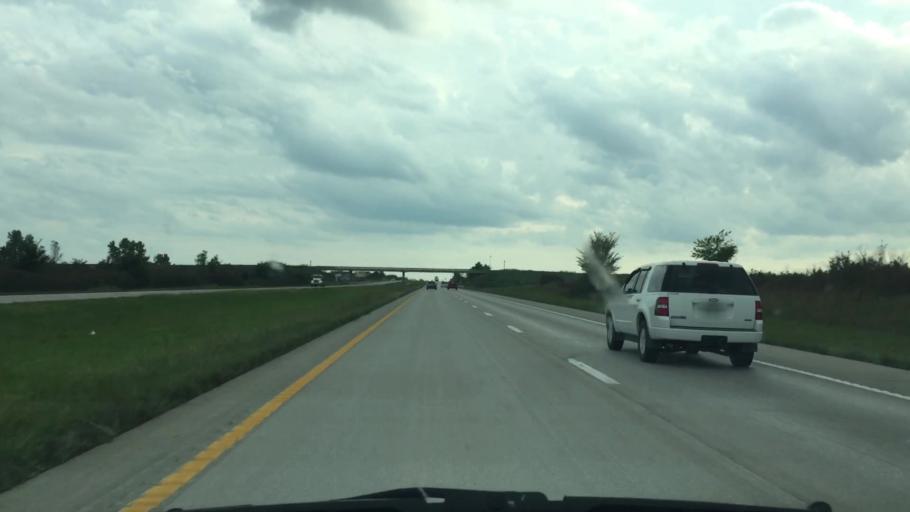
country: US
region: Missouri
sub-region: Clinton County
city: Cameron
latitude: 39.6360
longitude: -94.2439
